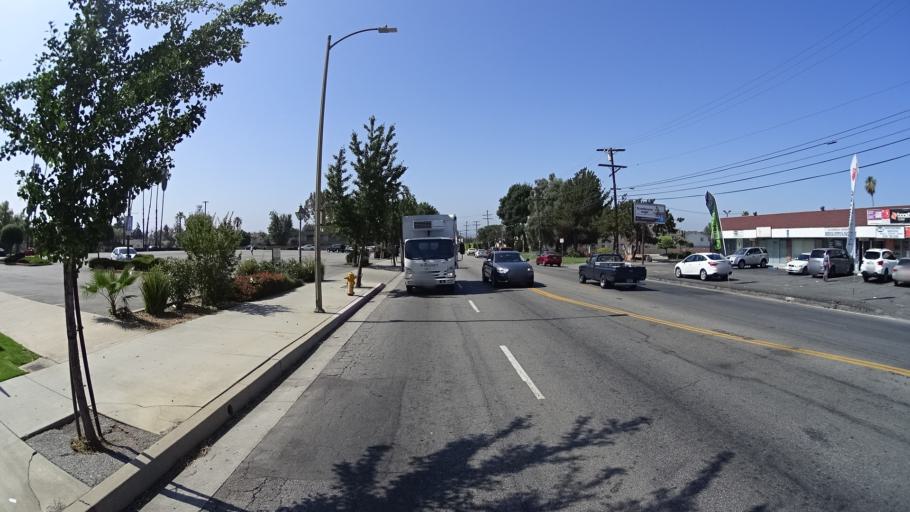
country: US
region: California
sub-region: Los Angeles County
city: Van Nuys
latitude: 34.2005
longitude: -118.4574
